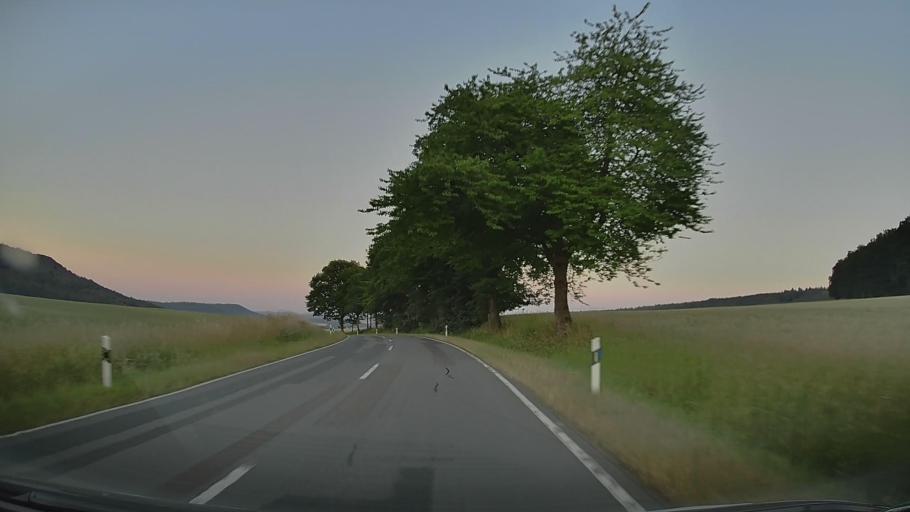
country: DE
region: Lower Saxony
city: Aerzen
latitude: 52.0222
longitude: 9.2884
